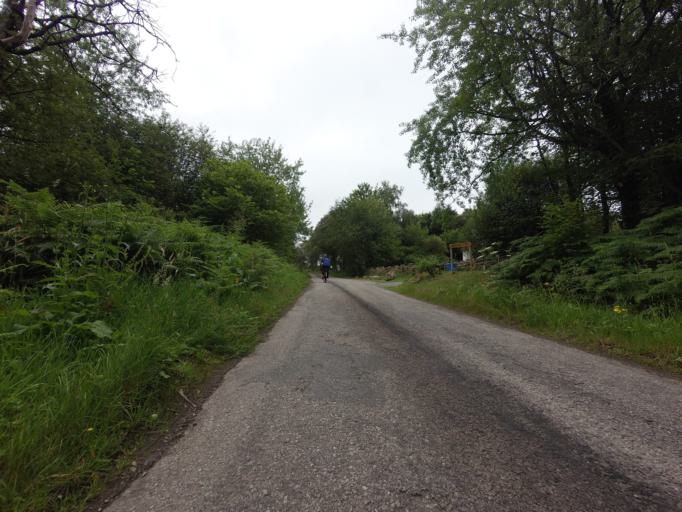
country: GB
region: Scotland
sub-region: Highland
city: Evanton
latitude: 57.9618
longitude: -4.4081
